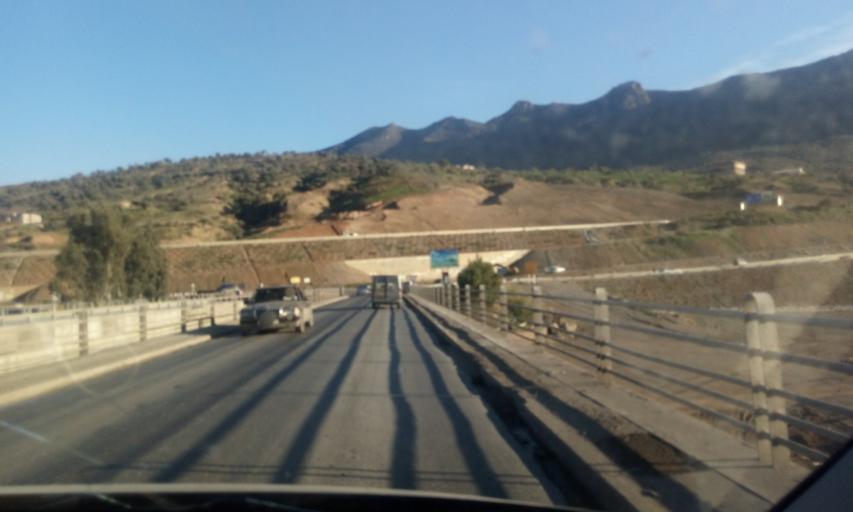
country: DZ
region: Bejaia
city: Akbou
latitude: 36.4807
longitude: 4.5930
